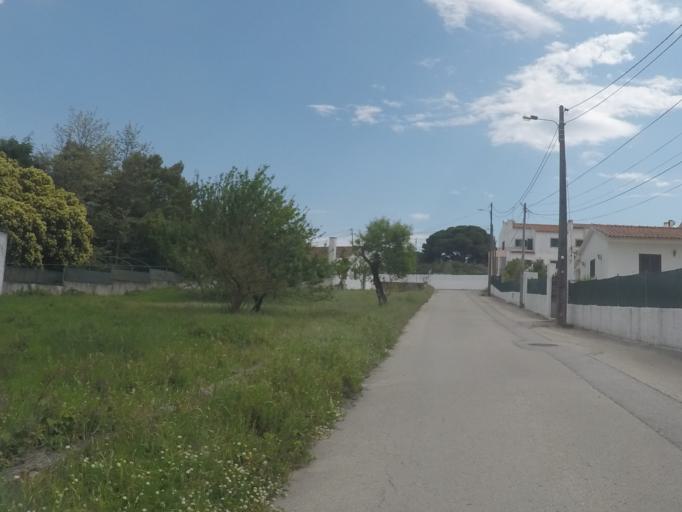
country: PT
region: Setubal
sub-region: Sesimbra
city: Sesimbra
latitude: 38.4616
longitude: -9.0743
